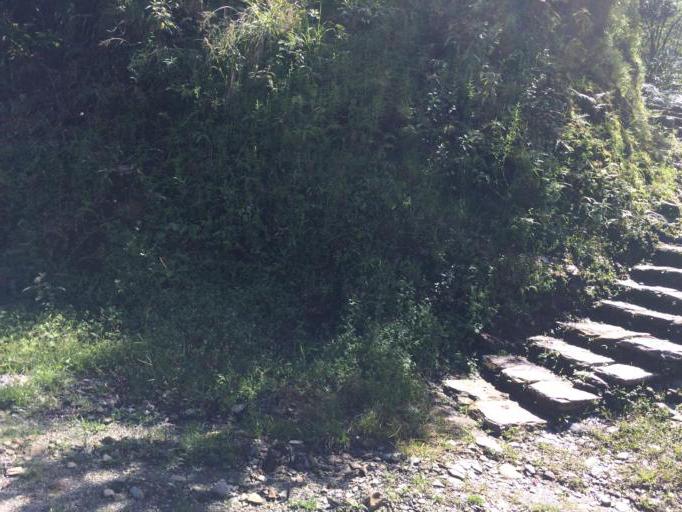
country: NP
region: Western Region
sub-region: Gandaki Zone
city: Pokhara
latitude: 28.2348
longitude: 83.8268
